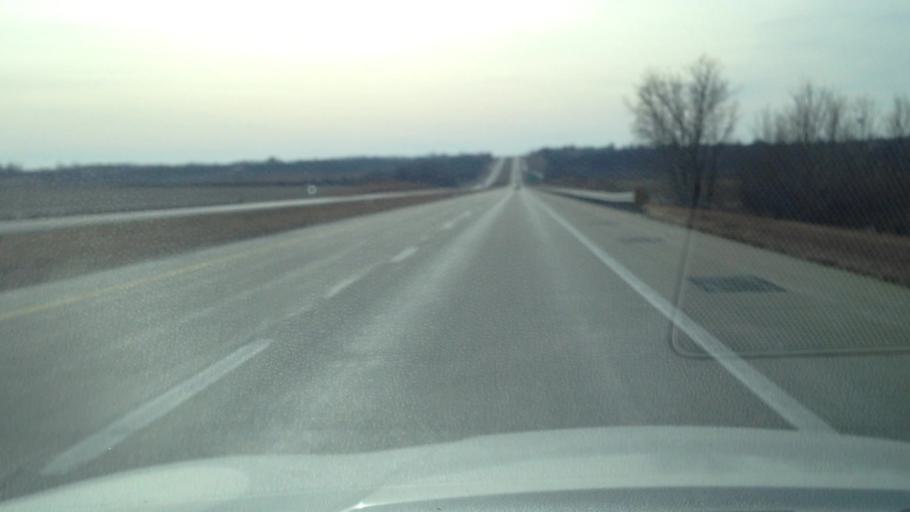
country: US
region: Missouri
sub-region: Harrison County
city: Bethany
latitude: 40.3028
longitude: -94.0122
